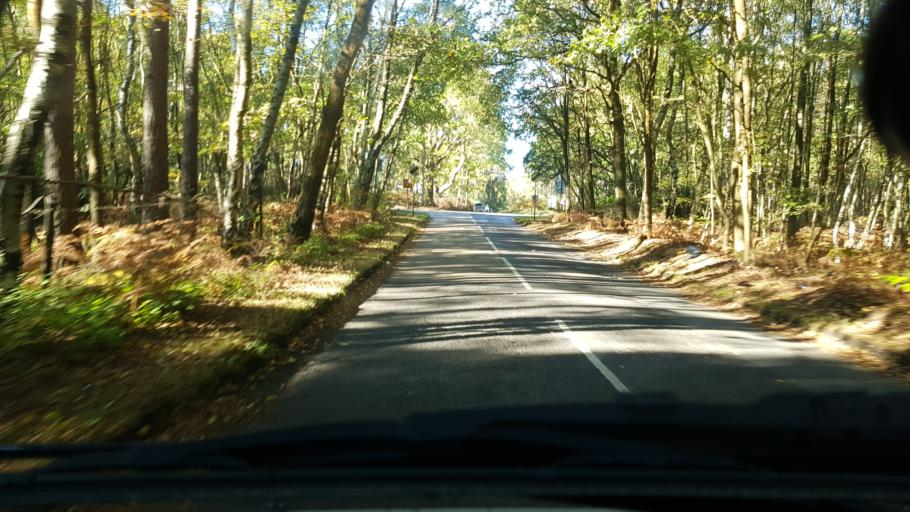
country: GB
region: England
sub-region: Surrey
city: Pirbright
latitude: 51.2729
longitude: -0.6540
